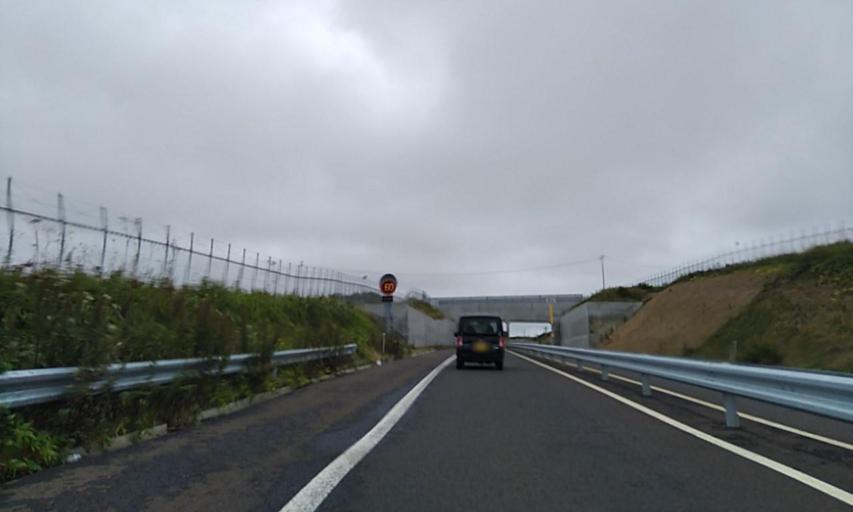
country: JP
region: Hokkaido
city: Nemuro
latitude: 43.3117
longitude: 145.5448
